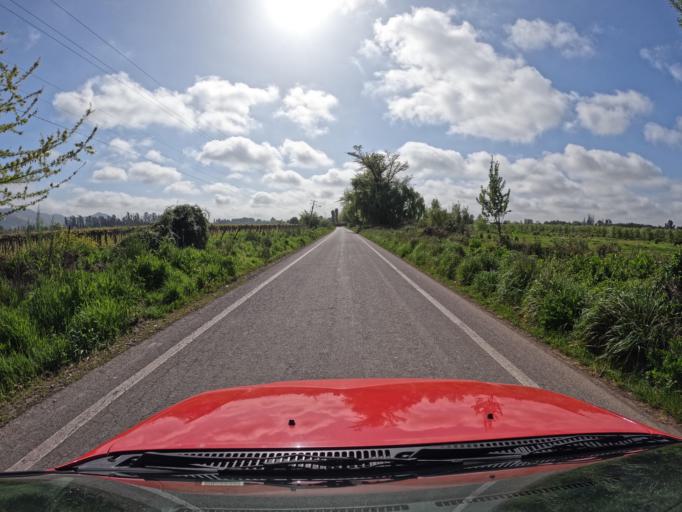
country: CL
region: Maule
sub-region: Provincia de Curico
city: Teno
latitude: -34.8798
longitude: -71.2353
